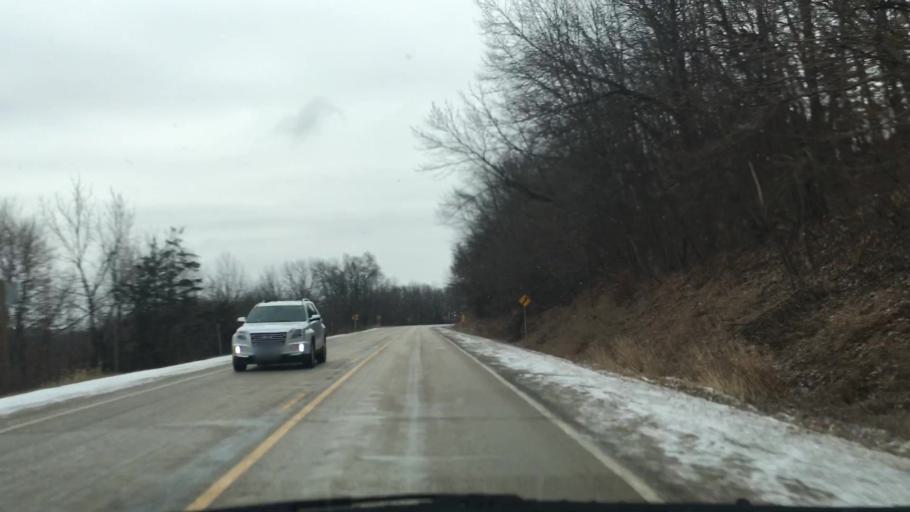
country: US
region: Iowa
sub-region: Fayette County
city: West Union
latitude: 43.0435
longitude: -91.8382
